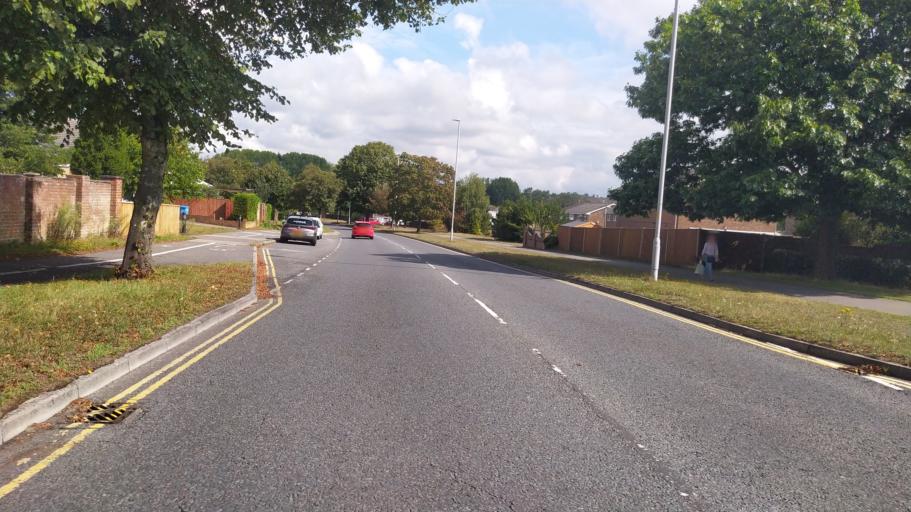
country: GB
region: England
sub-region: Poole
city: Canford Heath
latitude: 50.7446
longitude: -1.9629
